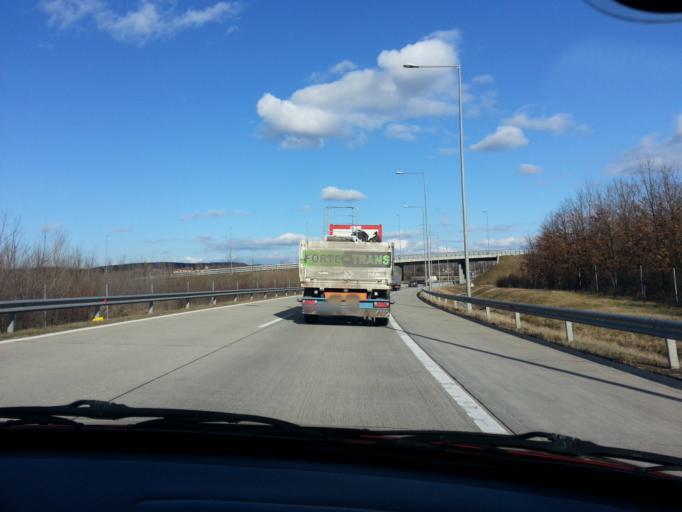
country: HU
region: Pest
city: Szada
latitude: 47.6115
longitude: 19.3197
